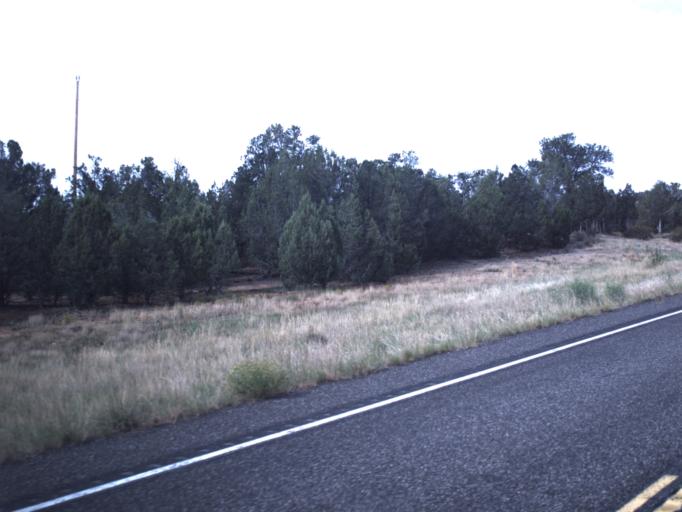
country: US
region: Utah
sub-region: Kane County
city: Kanab
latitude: 37.2203
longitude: -112.7056
